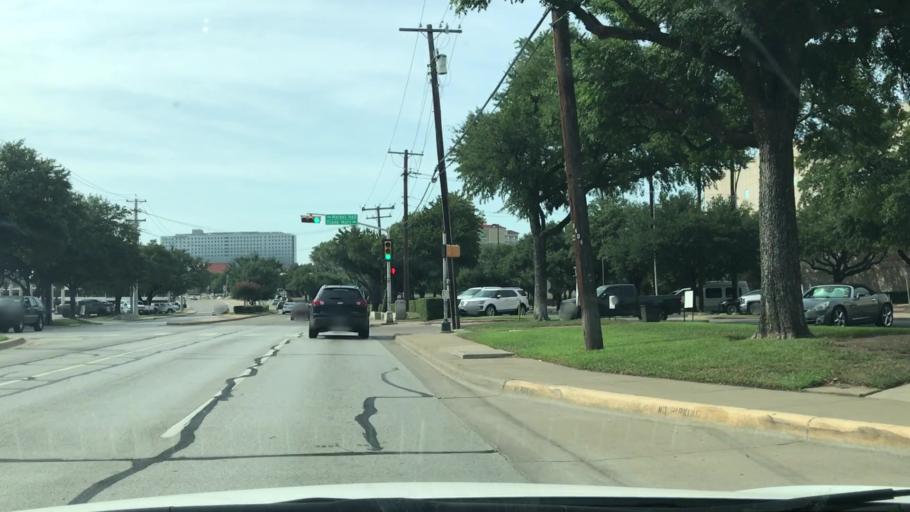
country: US
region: Texas
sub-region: Dallas County
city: Dallas
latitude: 32.8031
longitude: -96.8279
